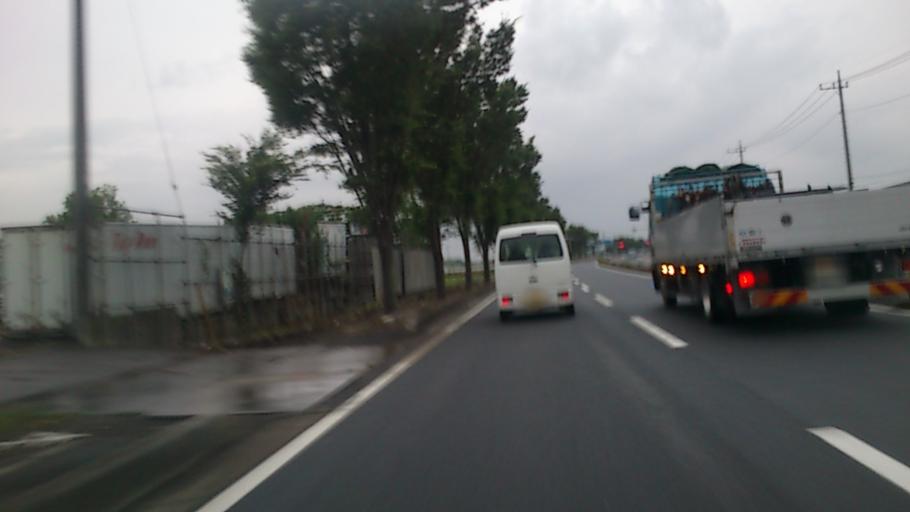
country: JP
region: Saitama
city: Hanyu
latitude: 36.1517
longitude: 139.5124
